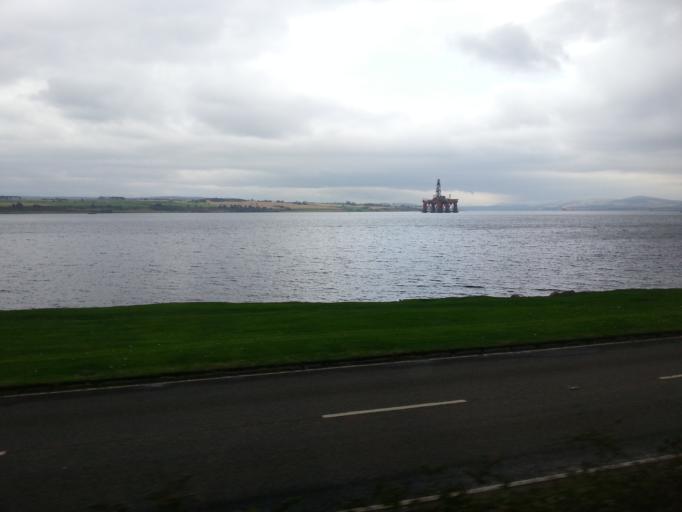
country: GB
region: Scotland
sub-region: Highland
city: Invergordon
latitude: 57.6907
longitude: -4.1855
